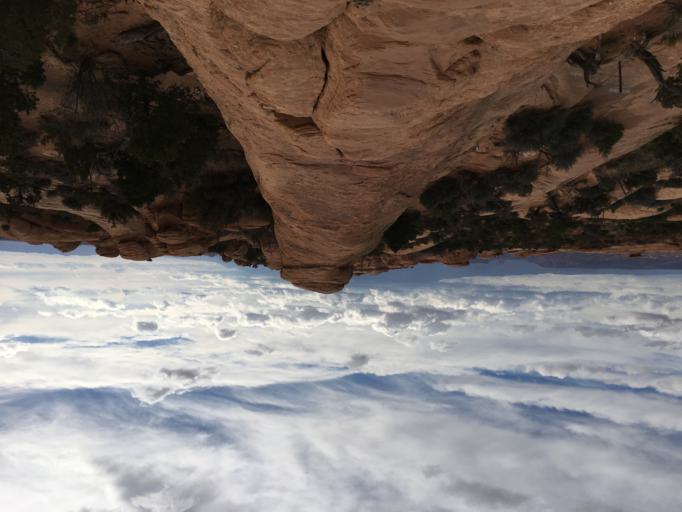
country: US
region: Utah
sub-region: Grand County
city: Moab
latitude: 38.7959
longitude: -109.6149
